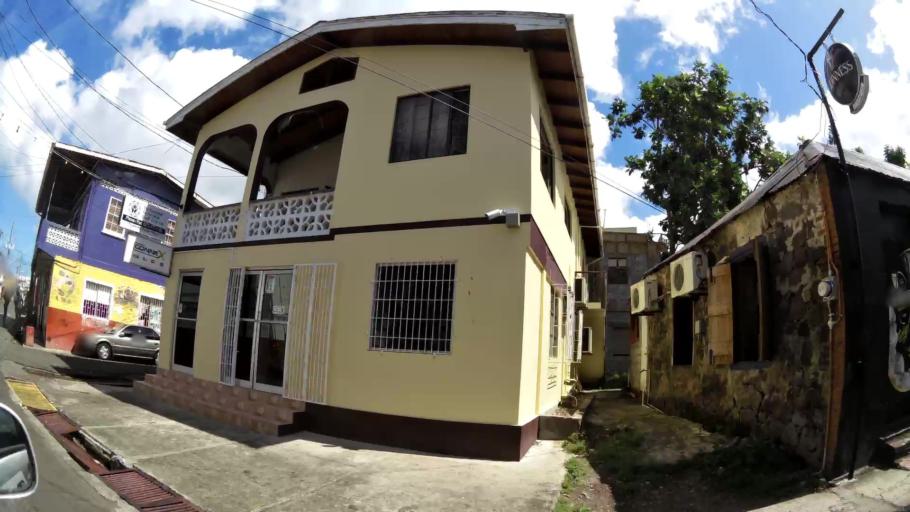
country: GD
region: Saint John
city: Gouyave
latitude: 12.1647
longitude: -61.7319
